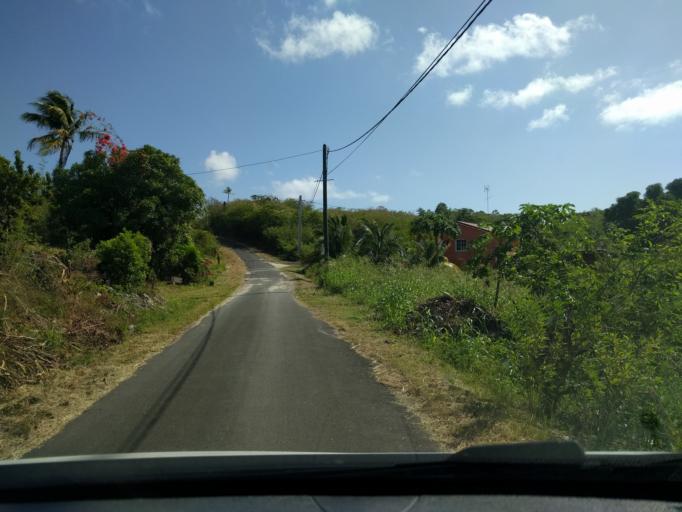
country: GP
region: Guadeloupe
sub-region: Guadeloupe
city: Grand-Bourg
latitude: 15.9765
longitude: -61.2556
